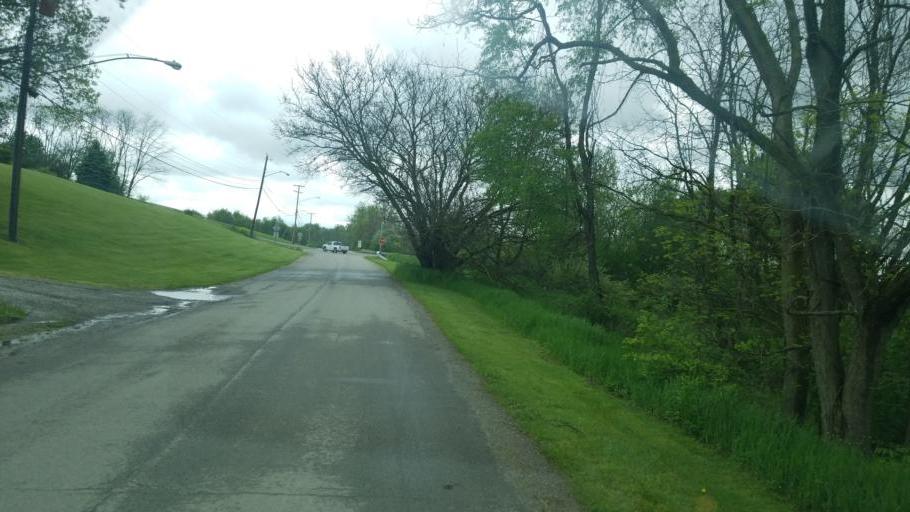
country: US
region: Ohio
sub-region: Harrison County
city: Cadiz
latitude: 40.2650
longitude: -81.0210
